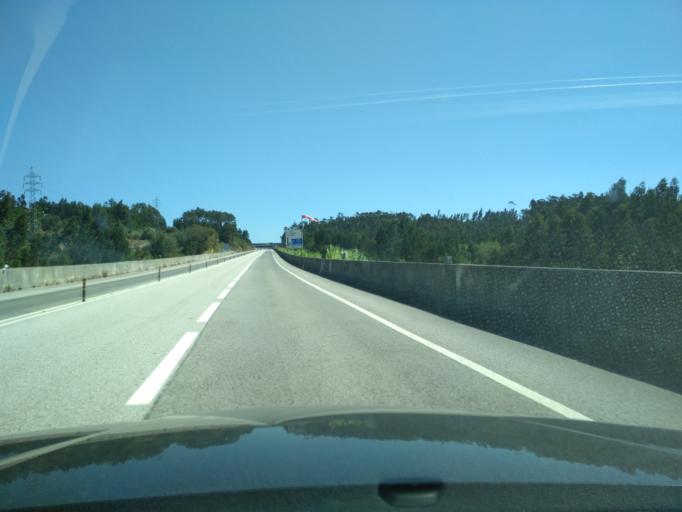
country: PT
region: Leiria
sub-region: Pombal
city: Pombal
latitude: 39.9486
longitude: -8.6821
